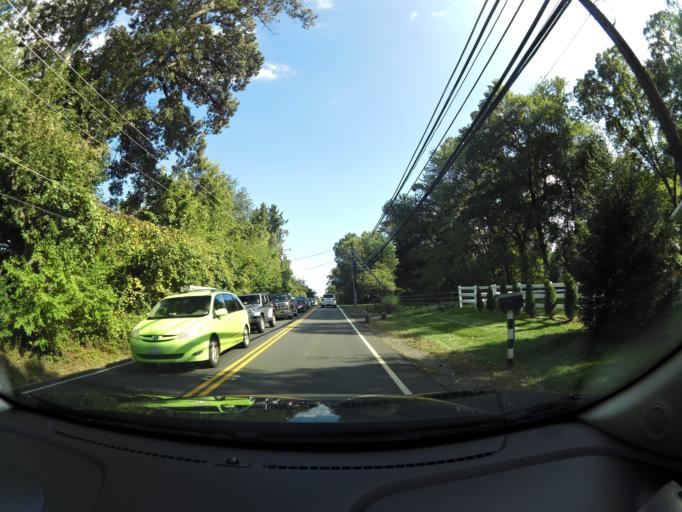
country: US
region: Virginia
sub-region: Fairfax County
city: Great Falls
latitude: 38.9964
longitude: -77.2845
